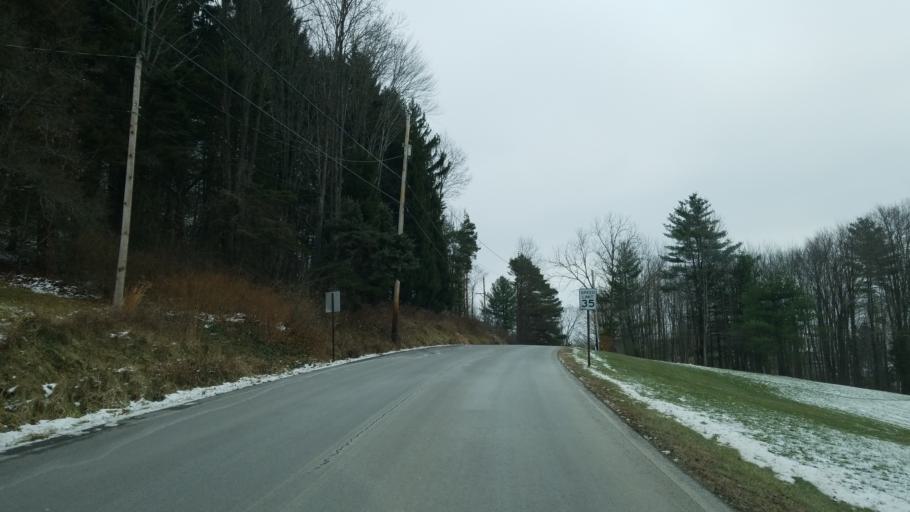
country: US
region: Pennsylvania
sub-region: Clearfield County
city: Sandy
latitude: 41.0953
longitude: -78.7530
